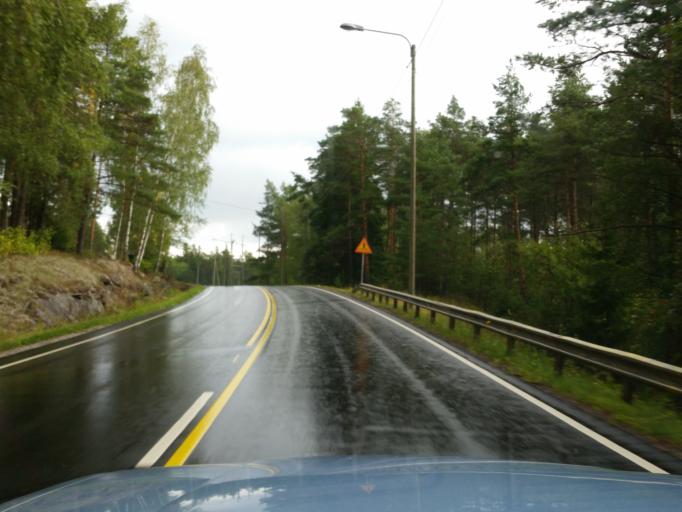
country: FI
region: Varsinais-Suomi
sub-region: Aboland-Turunmaa
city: Laensi-Turunmaa
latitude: 60.2872
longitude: 22.2593
